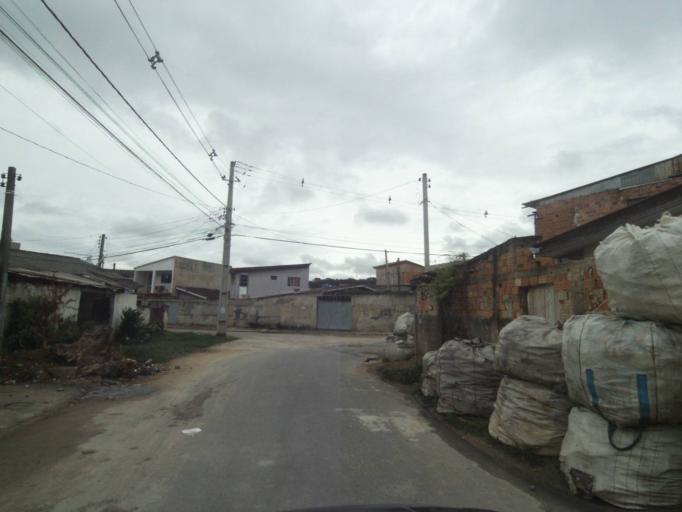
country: BR
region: Parana
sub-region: Curitiba
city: Curitiba
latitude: -25.4709
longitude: -49.3256
